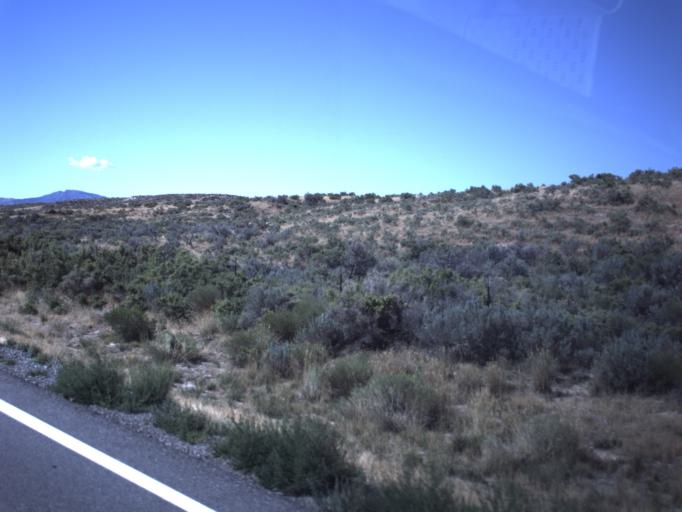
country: US
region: Utah
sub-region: Tooele County
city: Tooele
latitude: 40.1954
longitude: -112.4145
